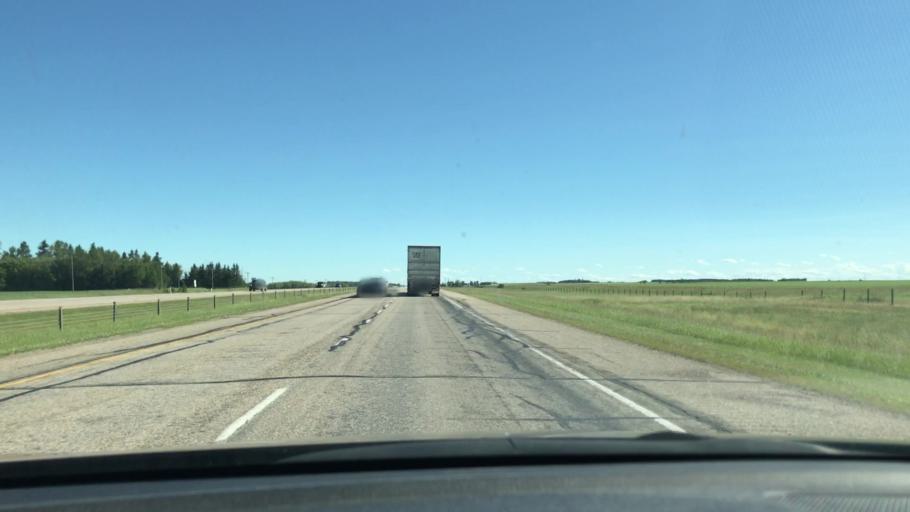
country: CA
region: Alberta
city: Olds
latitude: 51.8610
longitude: -114.0256
